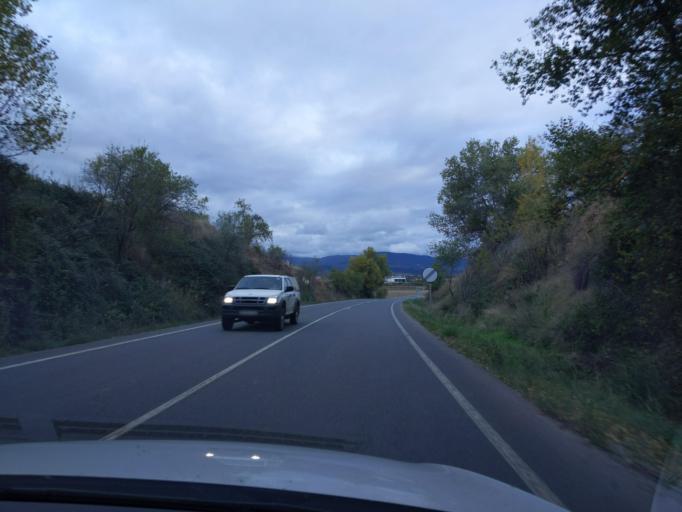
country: ES
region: La Rioja
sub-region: Provincia de La Rioja
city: Urunuela
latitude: 42.4446
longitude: -2.7002
